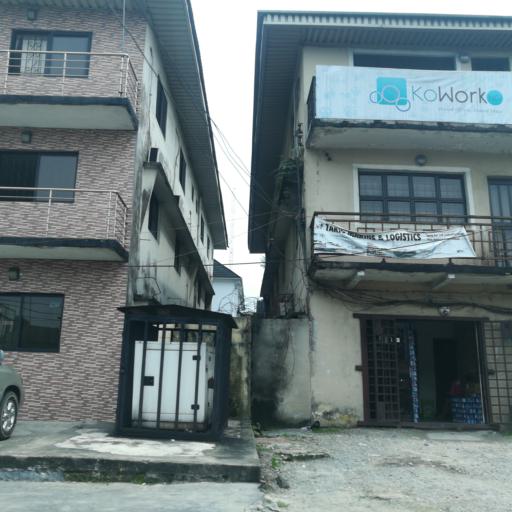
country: NG
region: Rivers
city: Port Harcourt
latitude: 4.8000
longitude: 7.0045
